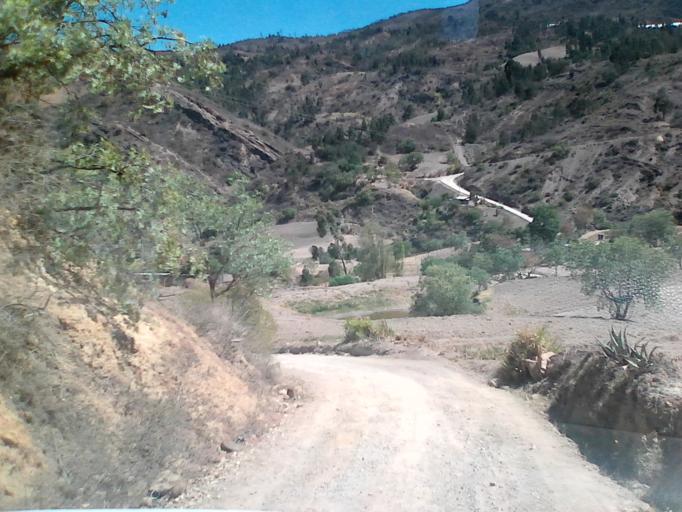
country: CO
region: Boyaca
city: Sachica
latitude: 5.5473
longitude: -73.5324
